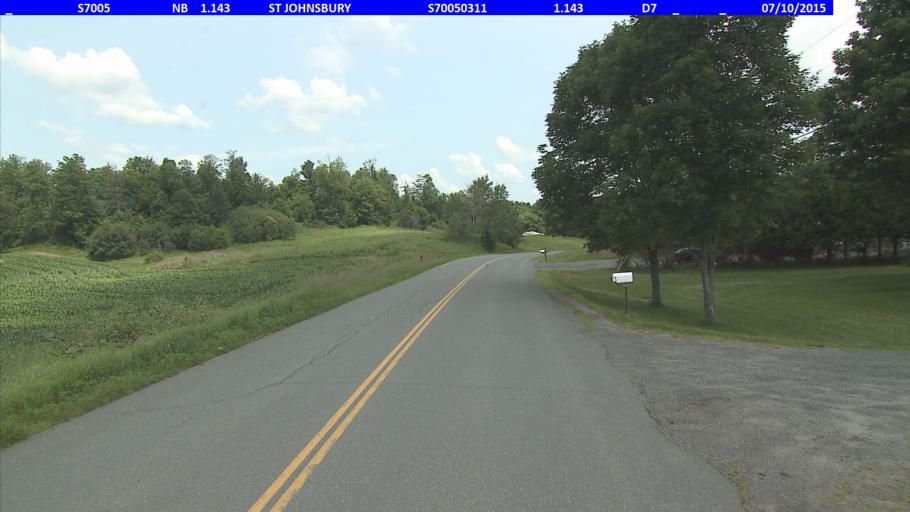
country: US
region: Vermont
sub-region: Caledonia County
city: St Johnsbury
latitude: 44.4499
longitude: -72.0068
